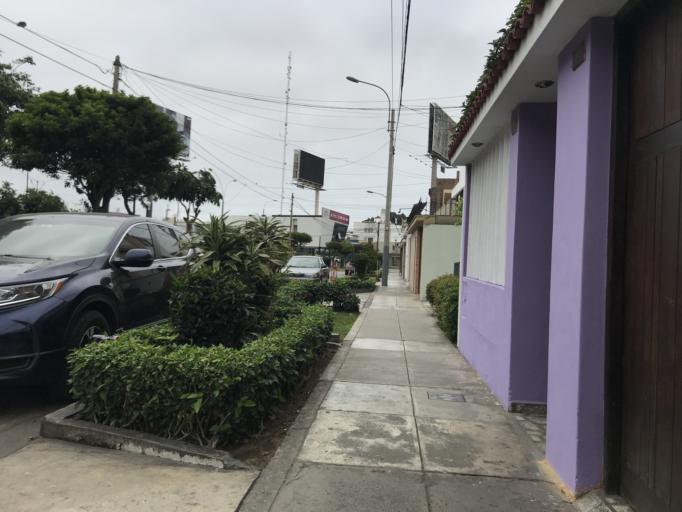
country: PE
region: Lima
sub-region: Lima
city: San Isidro
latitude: -12.0799
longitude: -77.0727
